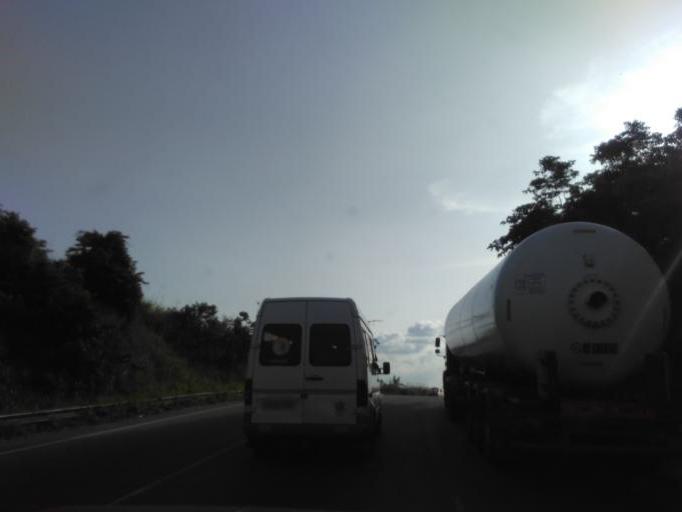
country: GH
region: Ashanti
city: Konongo
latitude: 6.6110
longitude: -1.2398
